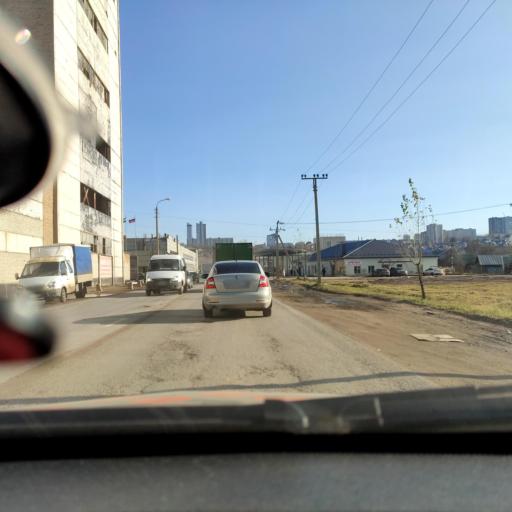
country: RU
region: Bashkortostan
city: Ufa
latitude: 54.7460
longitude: 55.9173
